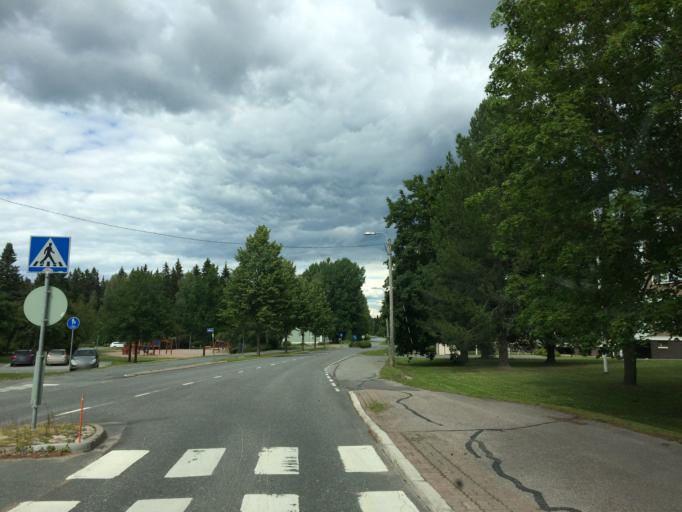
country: FI
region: Haeme
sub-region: Haemeenlinna
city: Tervakoski
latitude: 60.8174
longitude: 24.6226
